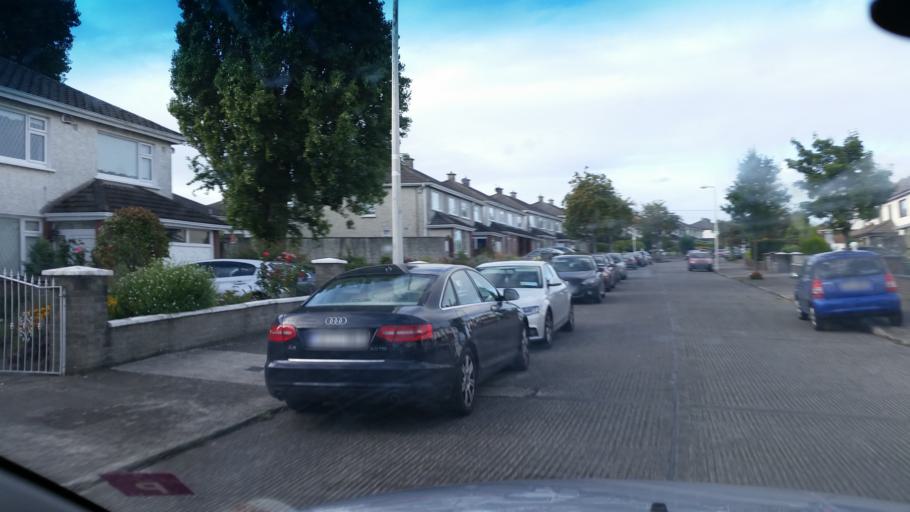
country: IE
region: Leinster
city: Drumcondra
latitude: 53.3783
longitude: -6.2529
